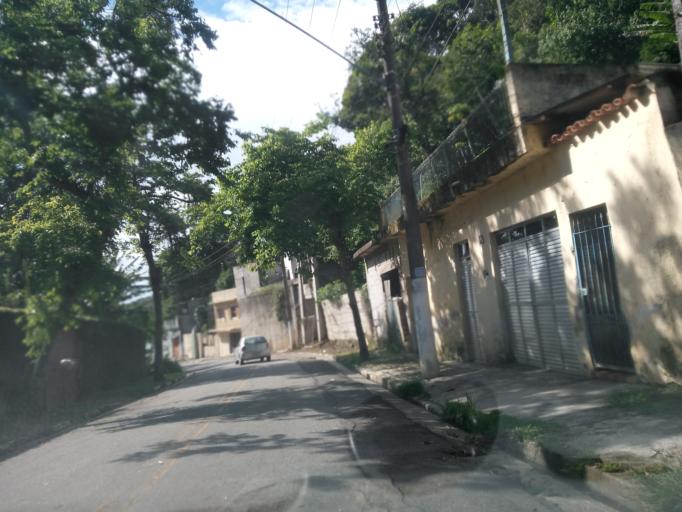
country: BR
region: Sao Paulo
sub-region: Sao Bernardo Do Campo
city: Sao Bernardo do Campo
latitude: -23.7984
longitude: -46.5333
